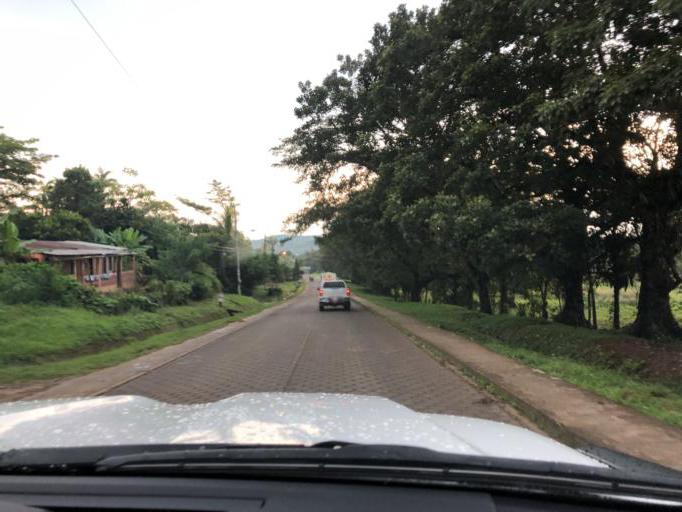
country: NI
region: Chontales
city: La Libertad
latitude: 12.2118
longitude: -85.1753
